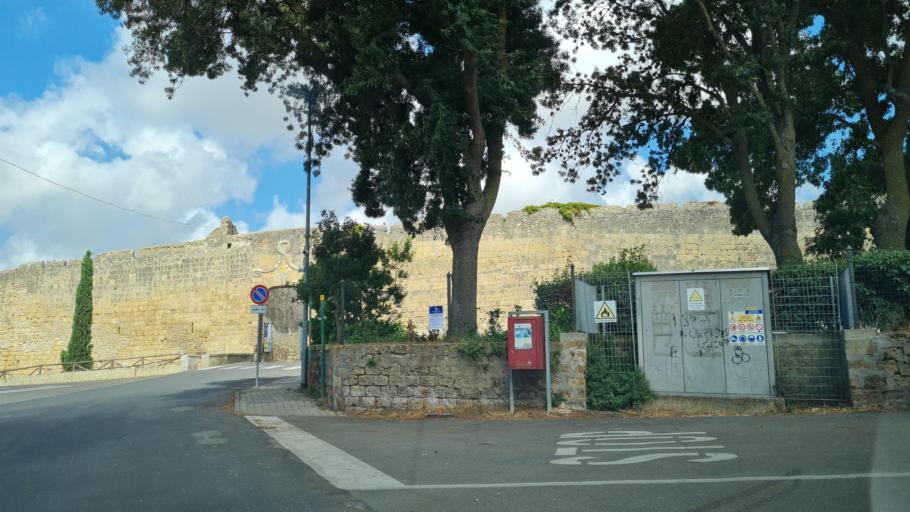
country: IT
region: Latium
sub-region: Provincia di Viterbo
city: Tarquinia
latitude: 42.2524
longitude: 11.7615
